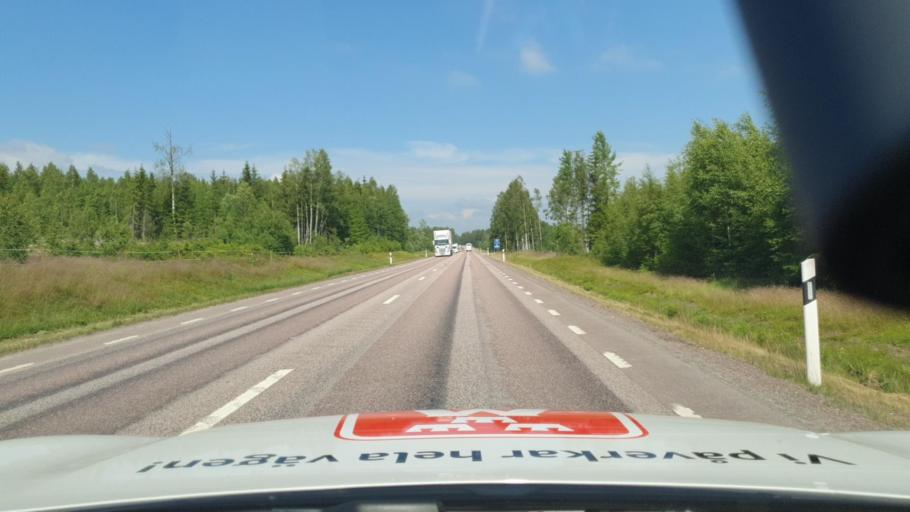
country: SE
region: Vaermland
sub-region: Torsby Kommun
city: Torsby
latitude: 60.1058
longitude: 13.0200
